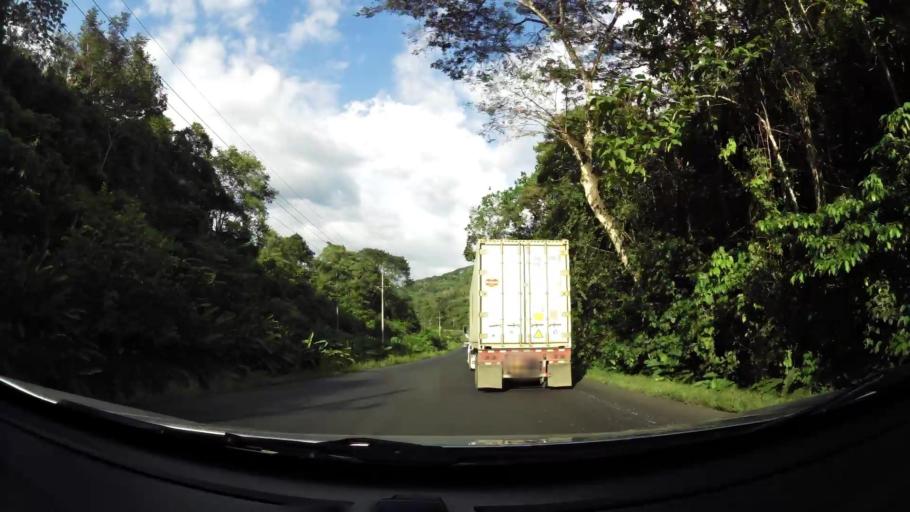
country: CR
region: Puntarenas
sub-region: Canton de Garabito
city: Jaco
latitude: 9.7705
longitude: -84.6099
